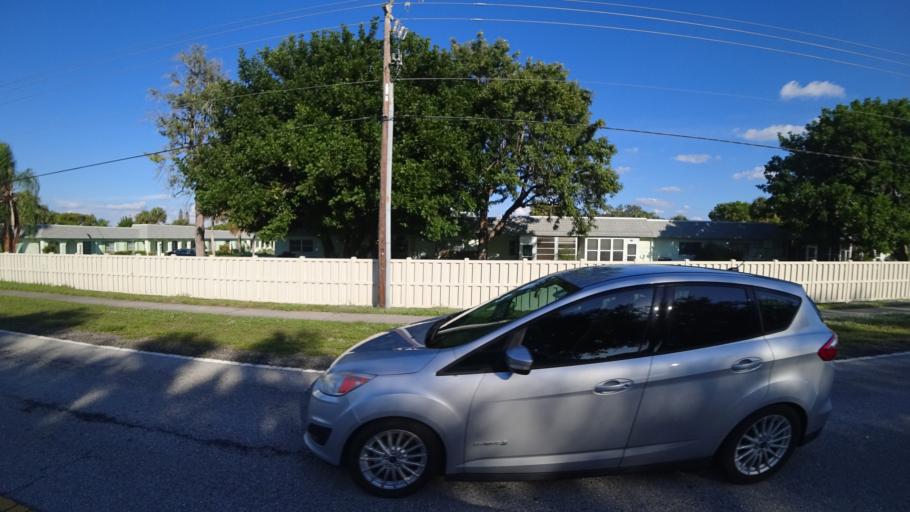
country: US
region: Florida
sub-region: Manatee County
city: South Bradenton
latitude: 27.4680
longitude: -82.6041
